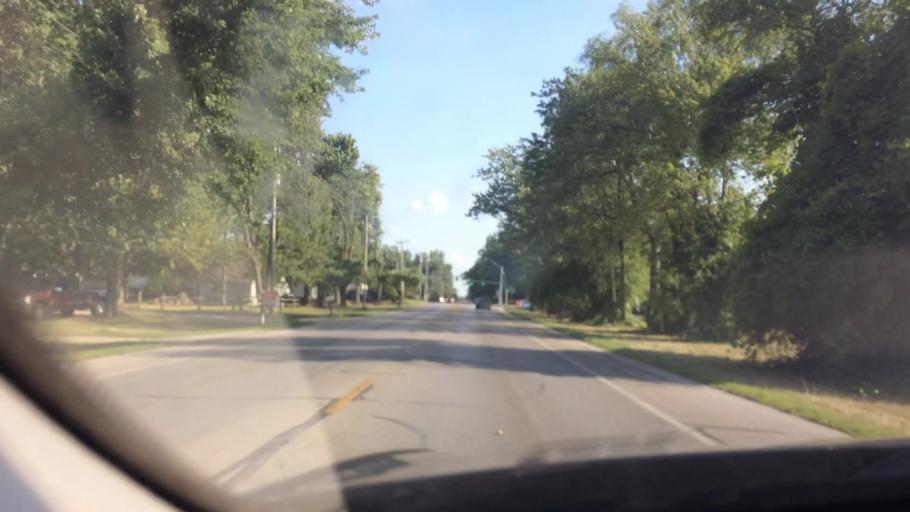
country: US
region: Ohio
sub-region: Lucas County
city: Holland
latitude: 41.6486
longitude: -83.7037
